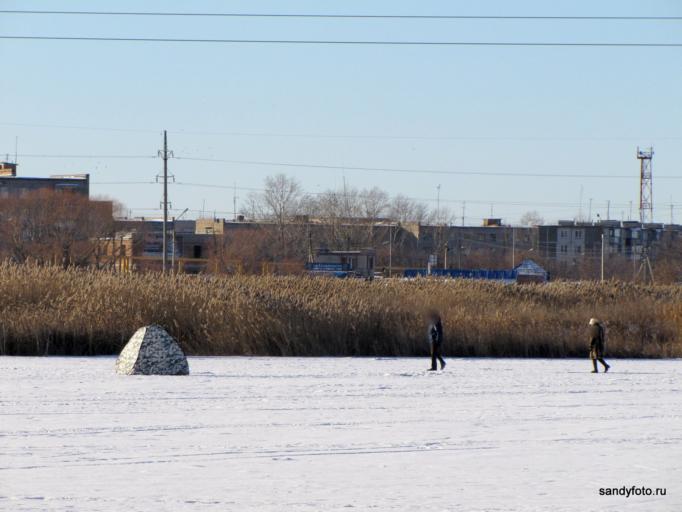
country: RU
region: Chelyabinsk
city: Troitsk
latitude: 54.0927
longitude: 61.5655
